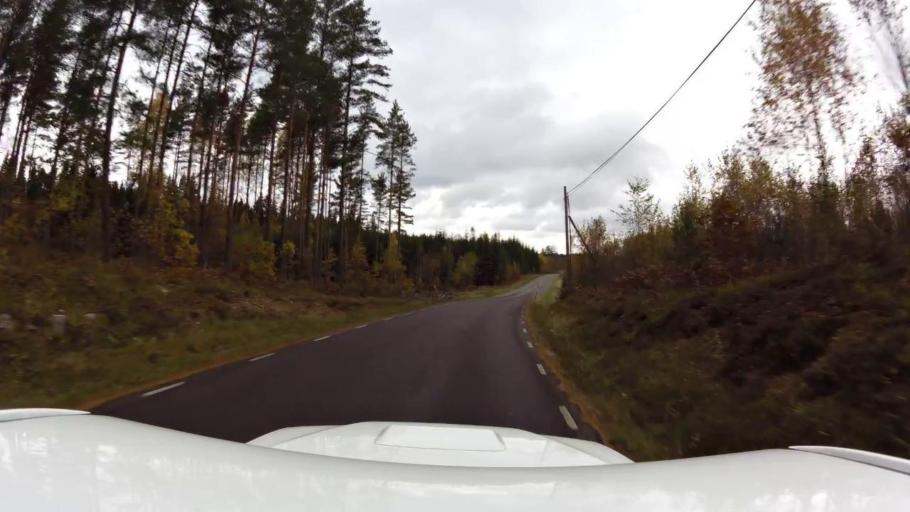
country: SE
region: OEstergoetland
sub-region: Motala Kommun
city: Borensberg
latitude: 58.5614
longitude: 15.3917
